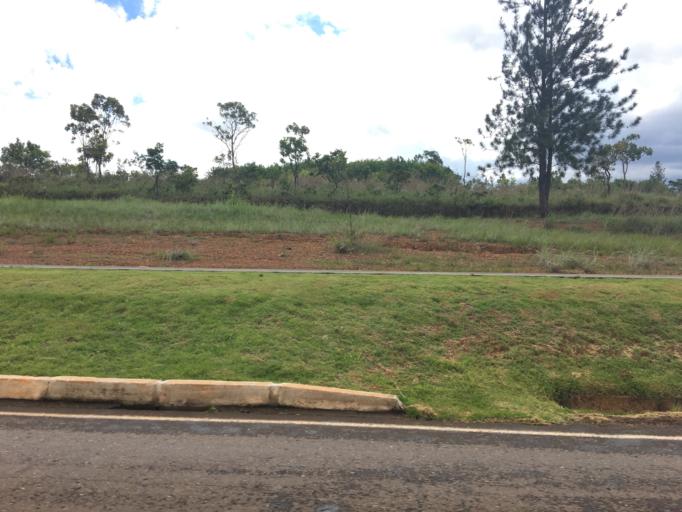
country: BR
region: Federal District
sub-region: Brasilia
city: Brasilia
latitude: -15.9011
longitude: -47.9151
